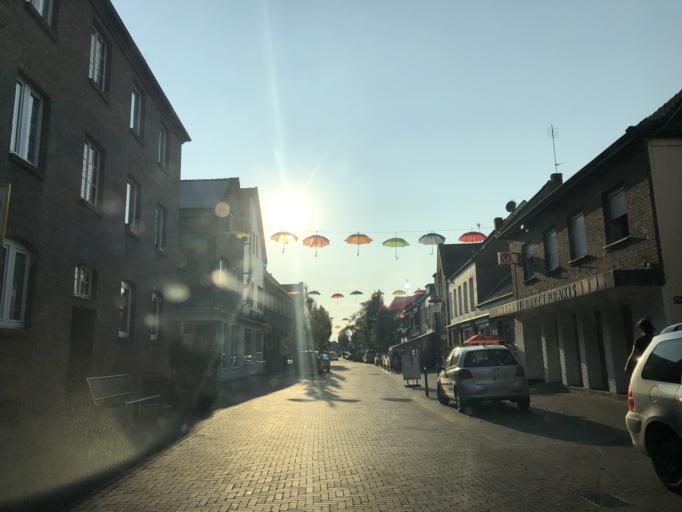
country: DE
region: North Rhine-Westphalia
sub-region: Regierungsbezirk Dusseldorf
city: Kranenburg
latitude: 51.7898
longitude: 6.0077
